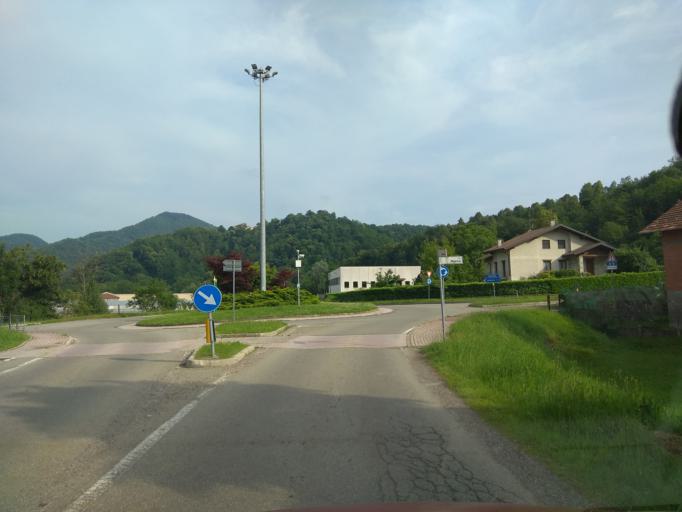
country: IT
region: Piedmont
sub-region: Provincia di Biella
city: Pray
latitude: 45.6756
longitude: 8.1988
